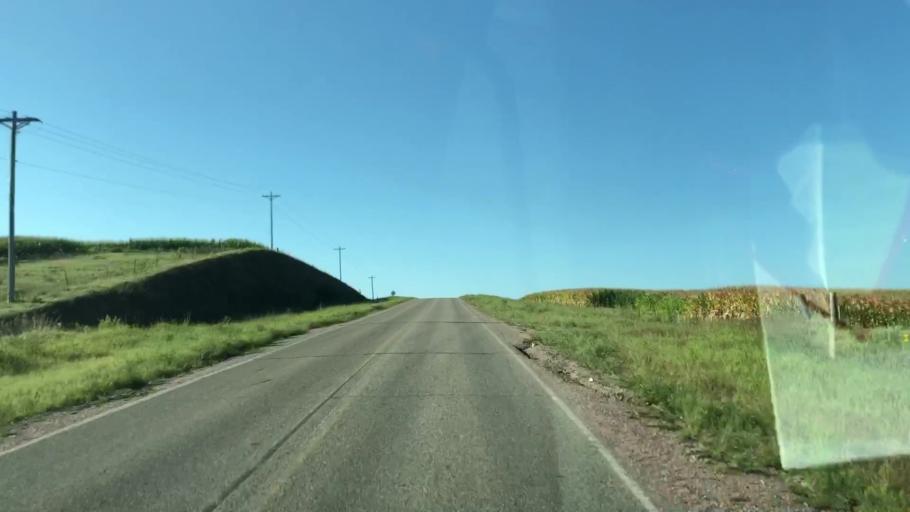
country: US
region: Iowa
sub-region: Woodbury County
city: Moville
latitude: 42.4744
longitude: -96.2136
